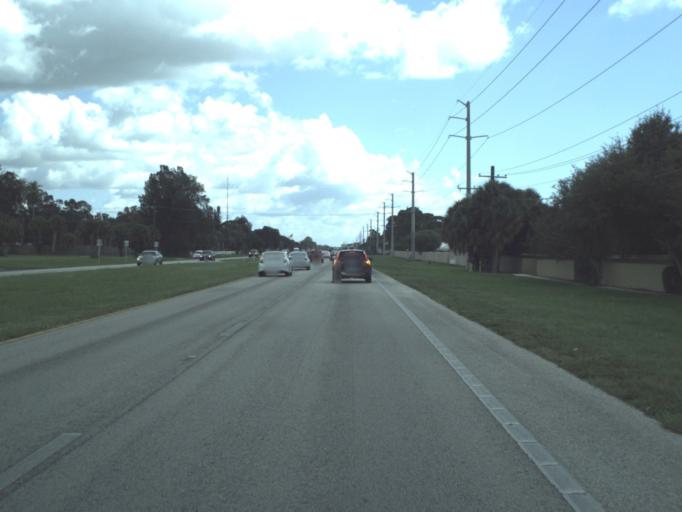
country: US
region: Florida
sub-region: Sarasota County
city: Laurel
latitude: 27.1647
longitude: -82.4754
